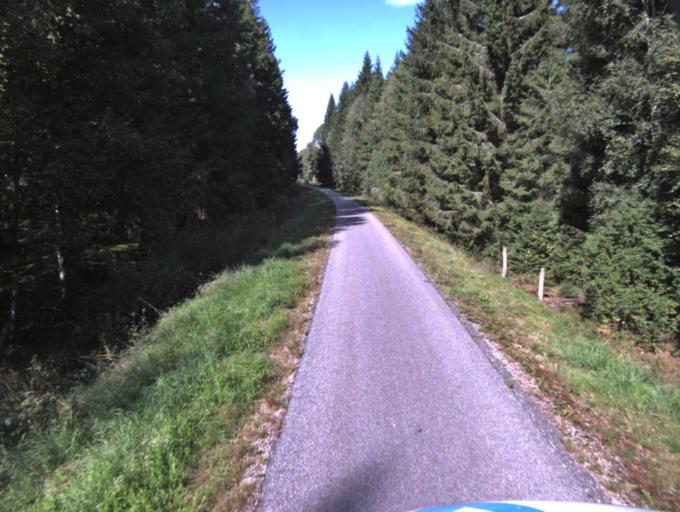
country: SE
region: Vaestra Goetaland
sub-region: Ulricehamns Kommun
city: Ulricehamn
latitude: 57.8287
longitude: 13.3452
